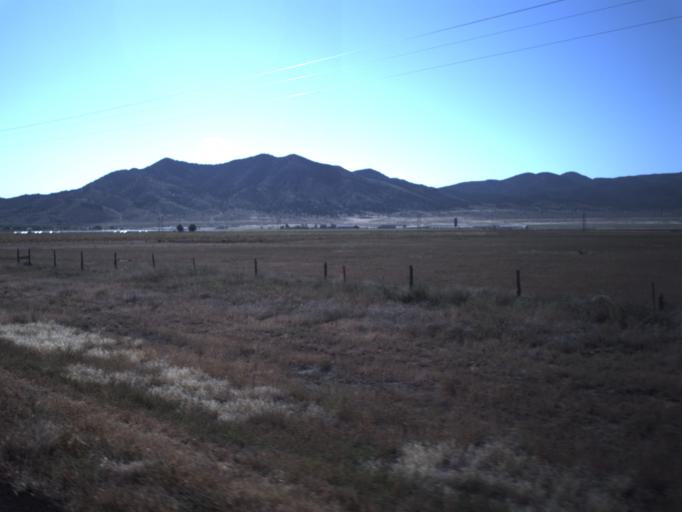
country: US
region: Utah
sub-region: Washington County
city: Enterprise
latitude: 37.6800
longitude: -113.5743
